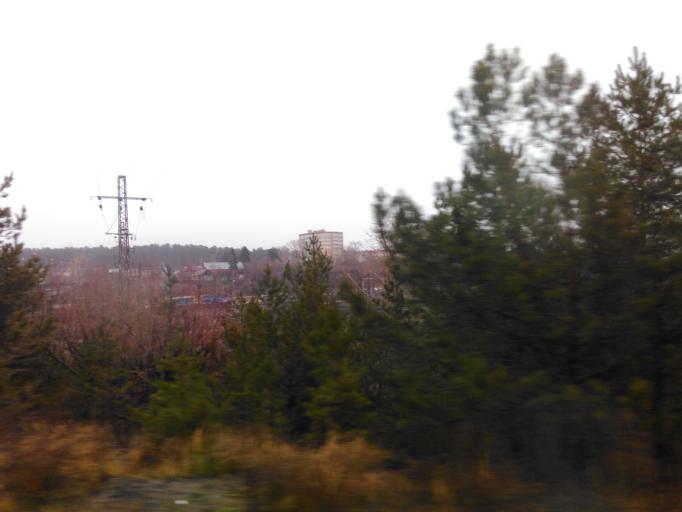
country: RU
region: Tatarstan
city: Osinovo
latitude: 55.8162
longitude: 48.8710
